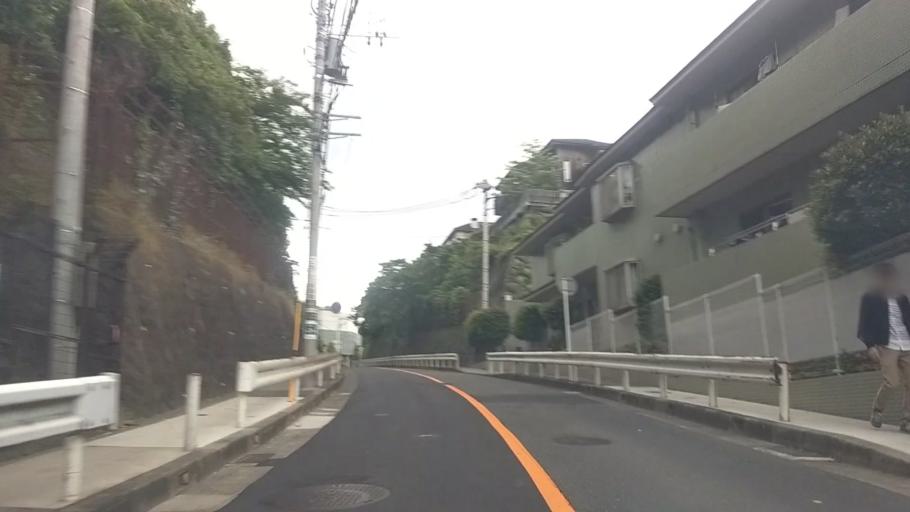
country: JP
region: Kanagawa
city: Fujisawa
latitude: 35.3559
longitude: 139.5223
